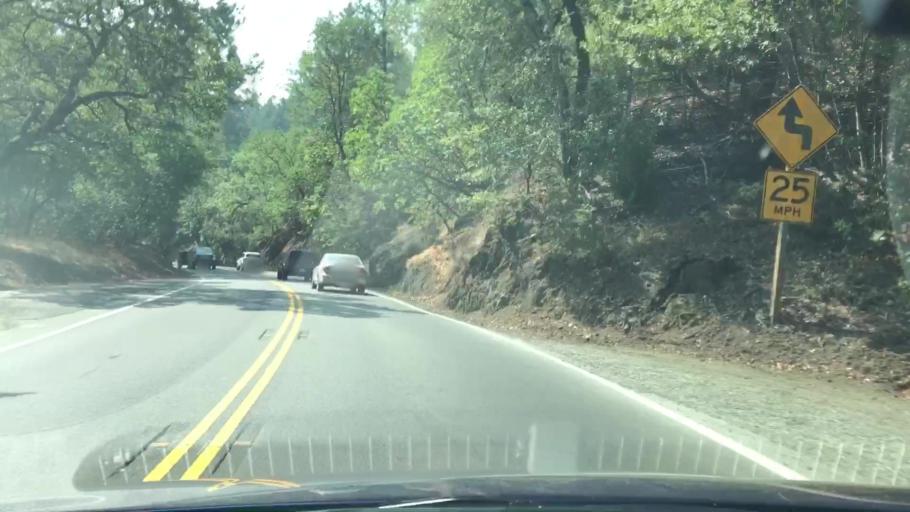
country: US
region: California
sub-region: Napa County
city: Calistoga
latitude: 38.6269
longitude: -122.6023
